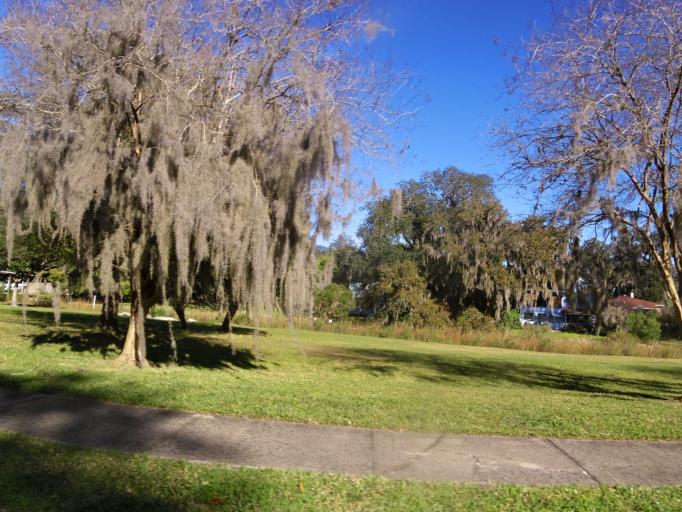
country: US
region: Florida
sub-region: Duval County
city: Jacksonville
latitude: 30.3876
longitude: -81.6505
